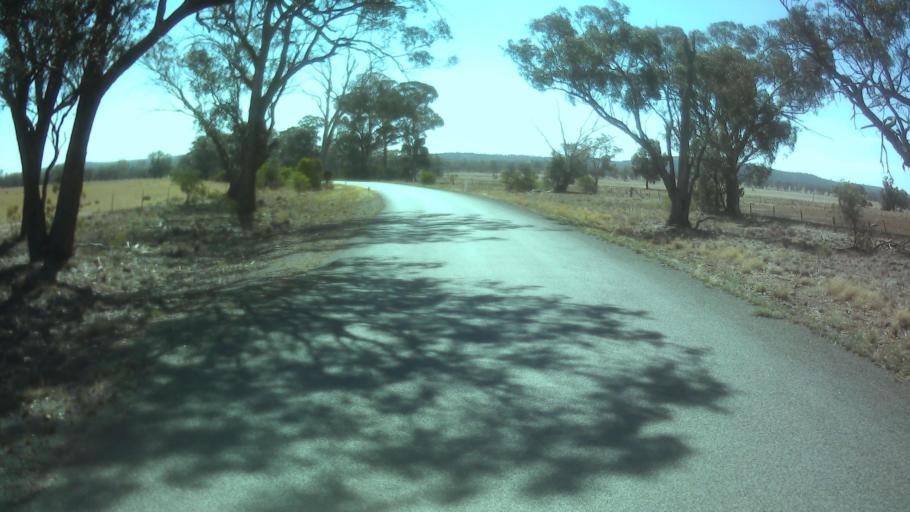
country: AU
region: New South Wales
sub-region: Weddin
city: Grenfell
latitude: -33.8092
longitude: 147.9114
